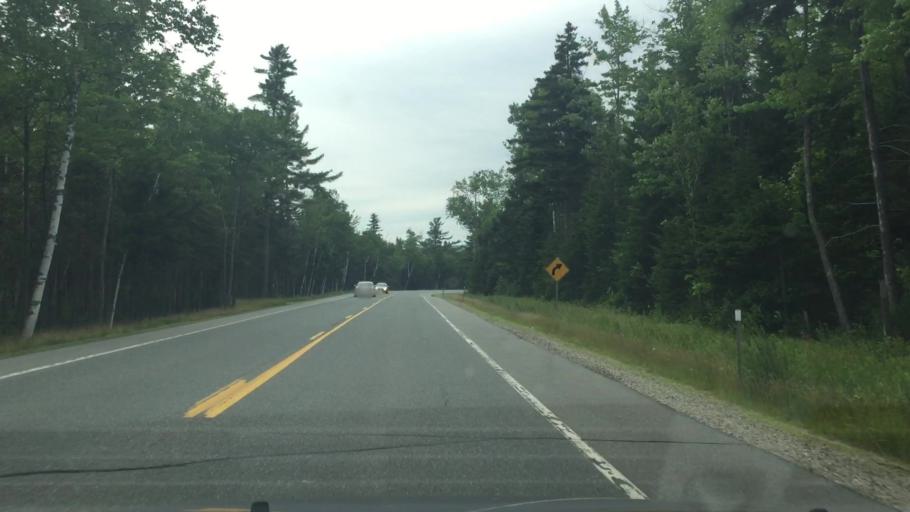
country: US
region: New Hampshire
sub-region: Grafton County
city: Deerfield
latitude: 44.2241
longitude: -71.6741
